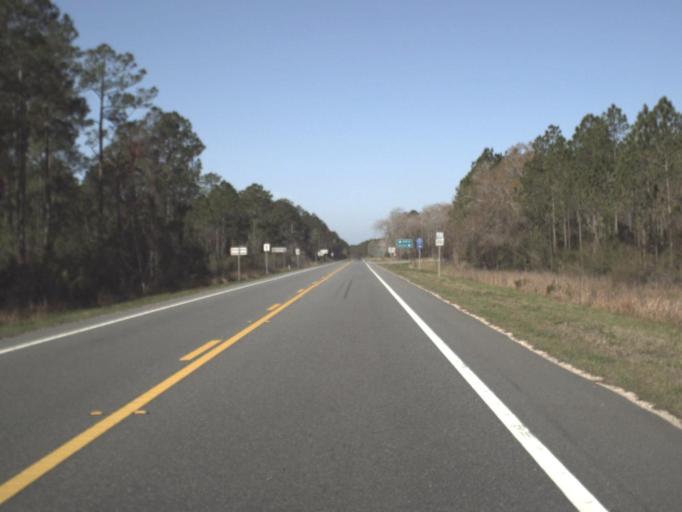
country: US
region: Florida
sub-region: Leon County
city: Woodville
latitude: 30.1894
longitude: -84.0474
